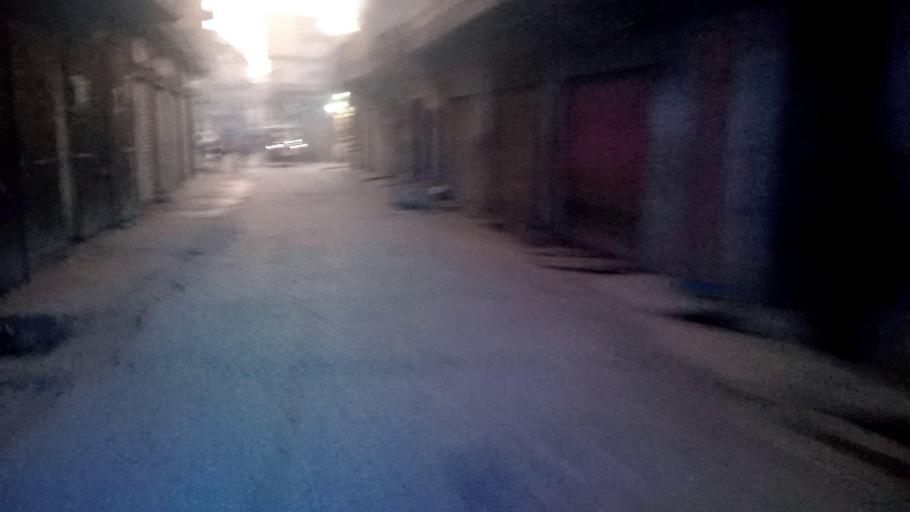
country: PK
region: Khyber Pakhtunkhwa
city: Mingora
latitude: 34.7773
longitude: 72.3541
